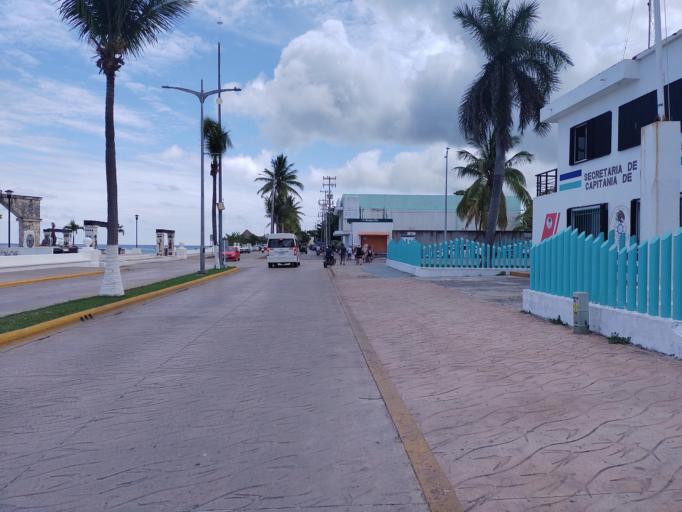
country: MX
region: Quintana Roo
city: San Miguel de Cozumel
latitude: 20.5163
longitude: -86.9458
